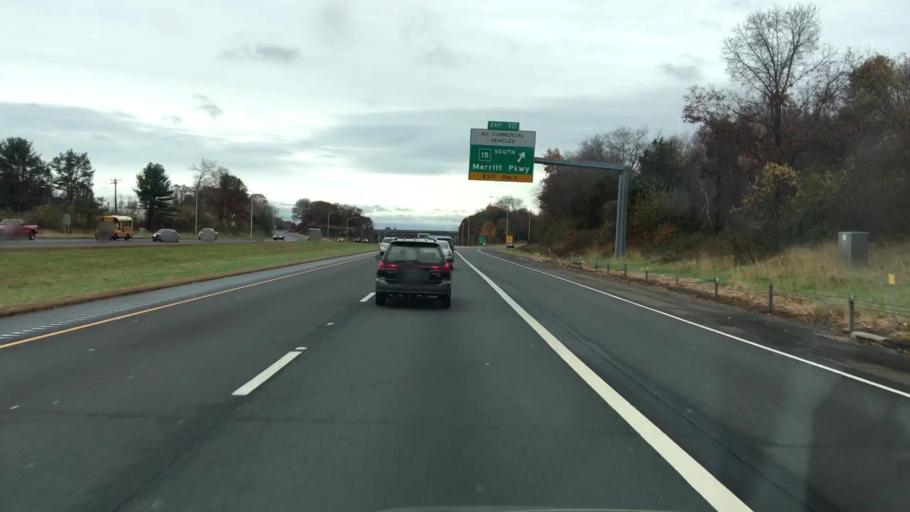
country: US
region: Connecticut
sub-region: Fairfield County
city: Trumbull
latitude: 41.2443
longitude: -73.1511
